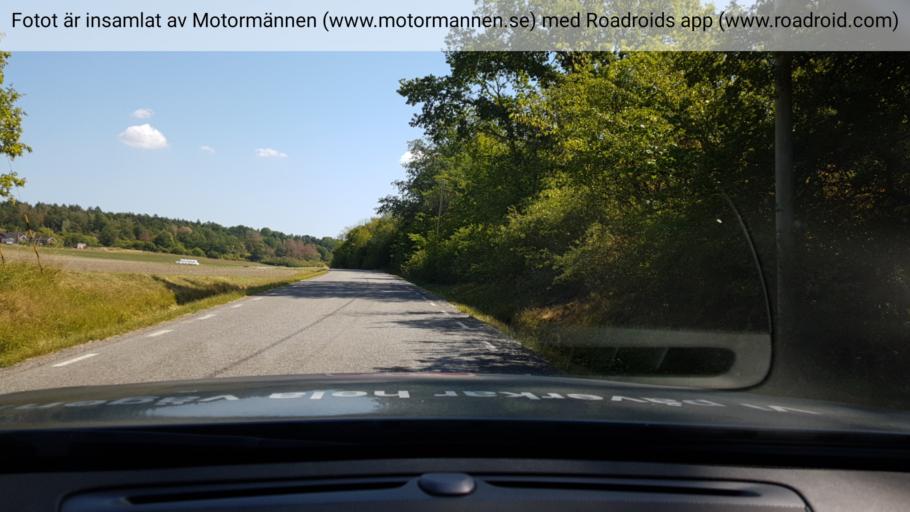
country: SE
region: Stockholm
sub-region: Upplands-Bro Kommun
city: Kungsaengen
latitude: 59.4070
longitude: 17.7077
